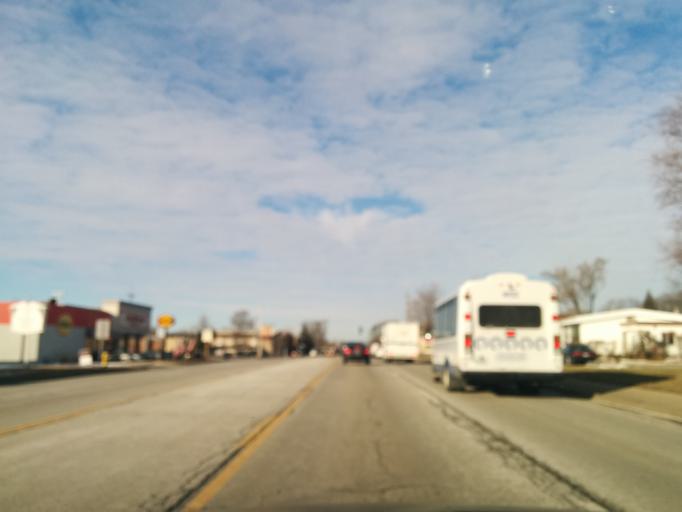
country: US
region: Illinois
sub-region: DuPage County
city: Wheaton
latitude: 41.8591
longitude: -88.0854
